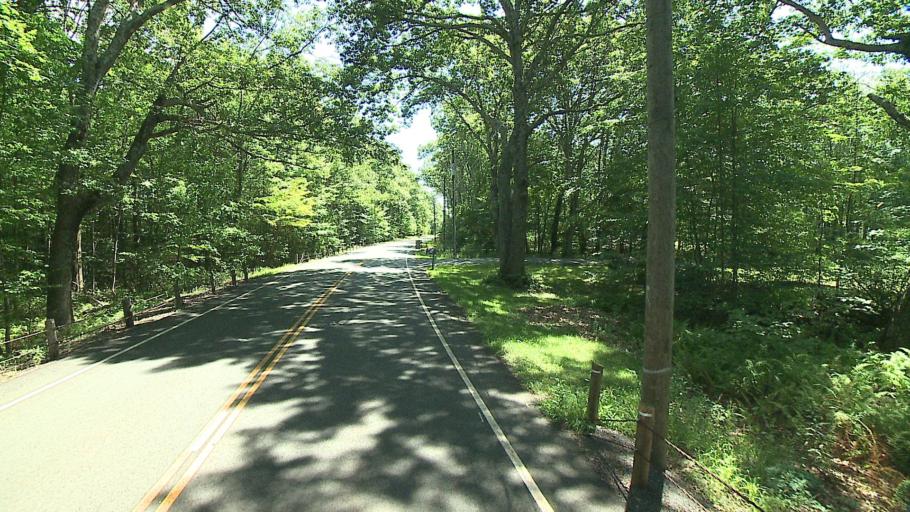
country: US
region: Connecticut
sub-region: Litchfield County
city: Winsted
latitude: 41.9828
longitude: -72.9822
